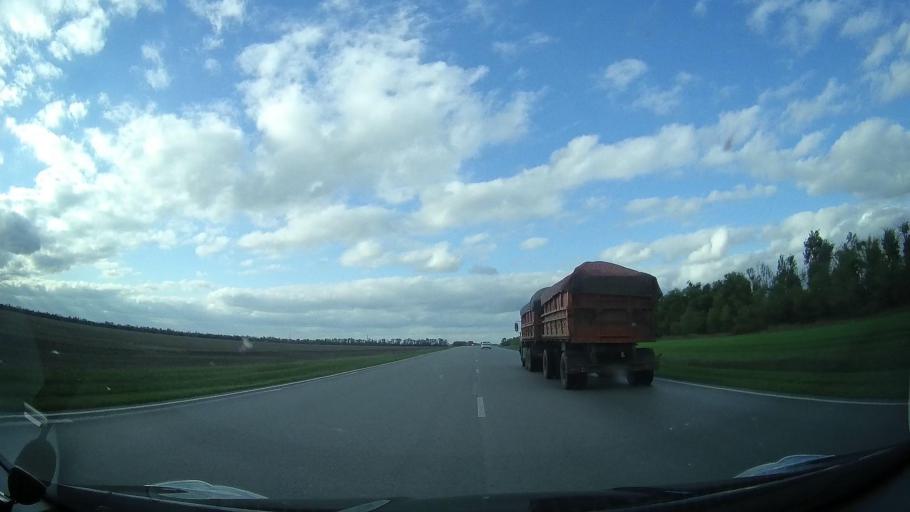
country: RU
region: Rostov
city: Kagal'nitskaya
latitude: 46.9227
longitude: 40.1028
